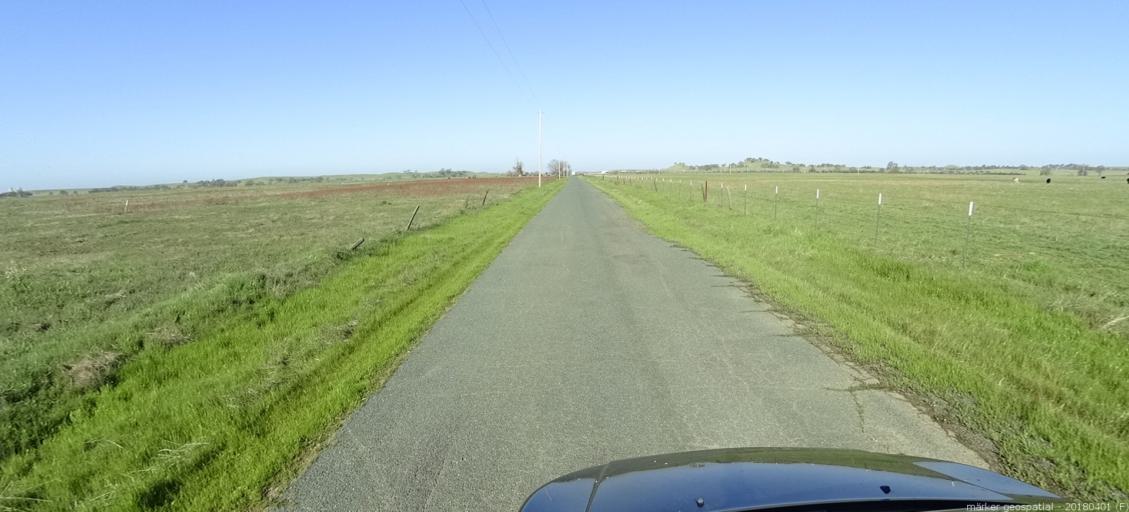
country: US
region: California
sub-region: Sacramento County
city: Rancho Murieta
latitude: 38.4204
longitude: -121.0395
